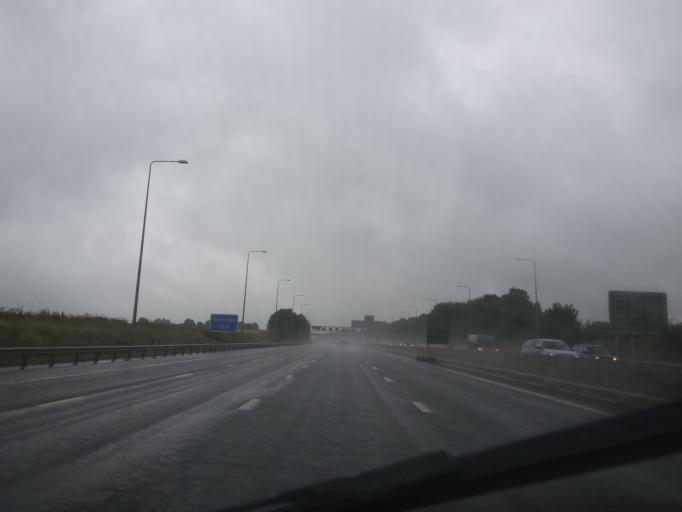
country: GB
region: England
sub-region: Derbyshire
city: Pinxton
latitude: 53.0862
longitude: -1.3012
